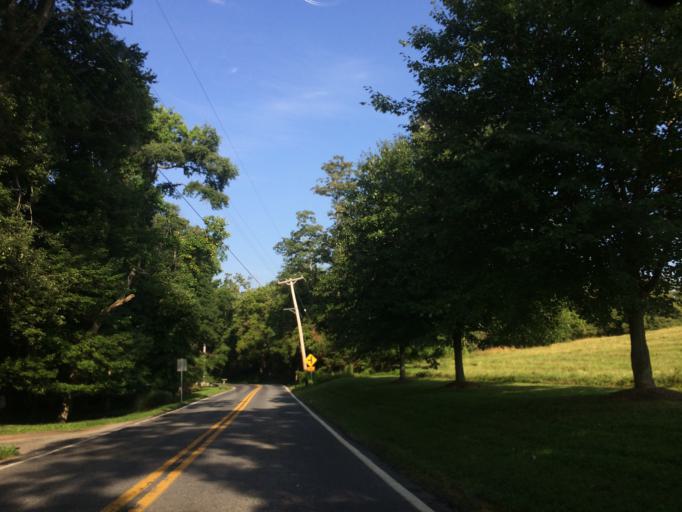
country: US
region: Maryland
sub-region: Carroll County
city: Sykesville
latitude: 39.3019
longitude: -77.0106
